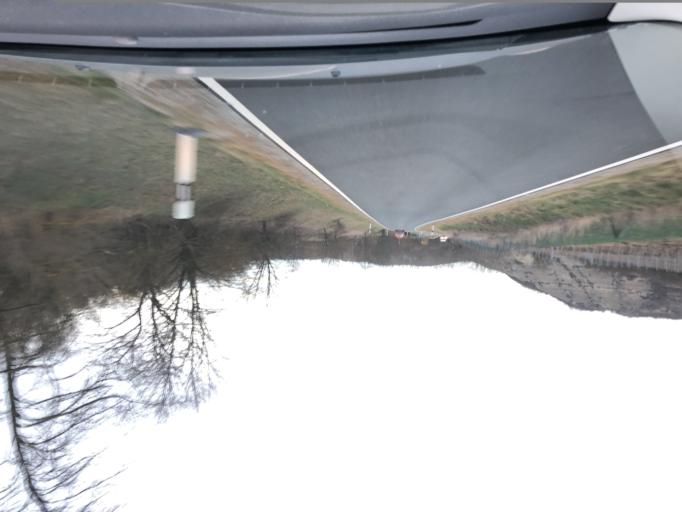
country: DE
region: Saxony-Anhalt
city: Balgstadt
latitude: 51.2067
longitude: 11.7242
